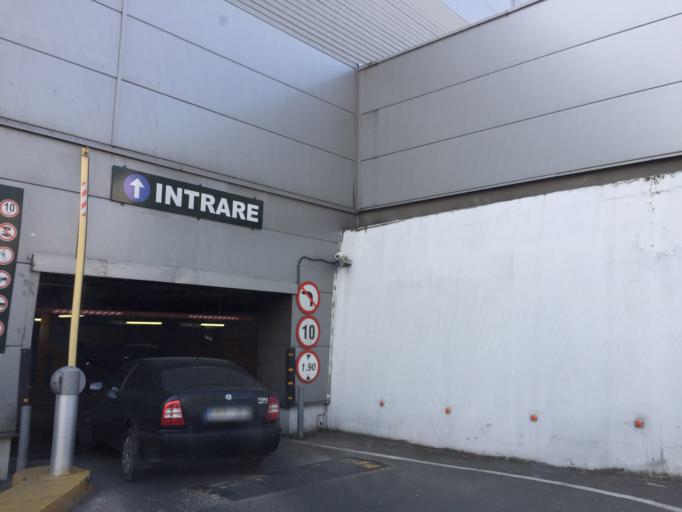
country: RO
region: Ilfov
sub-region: Comuna Popesti-Leordeni
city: Popesti-Leordeni
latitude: 44.4086
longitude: 26.1388
